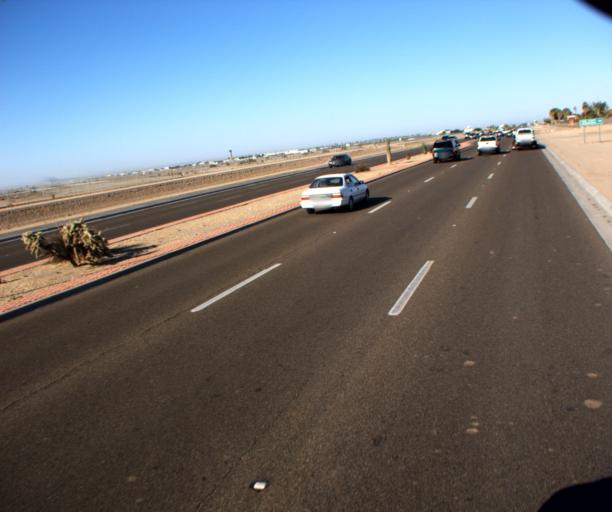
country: US
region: Arizona
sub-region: Yuma County
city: Yuma
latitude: 32.6697
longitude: -114.5881
